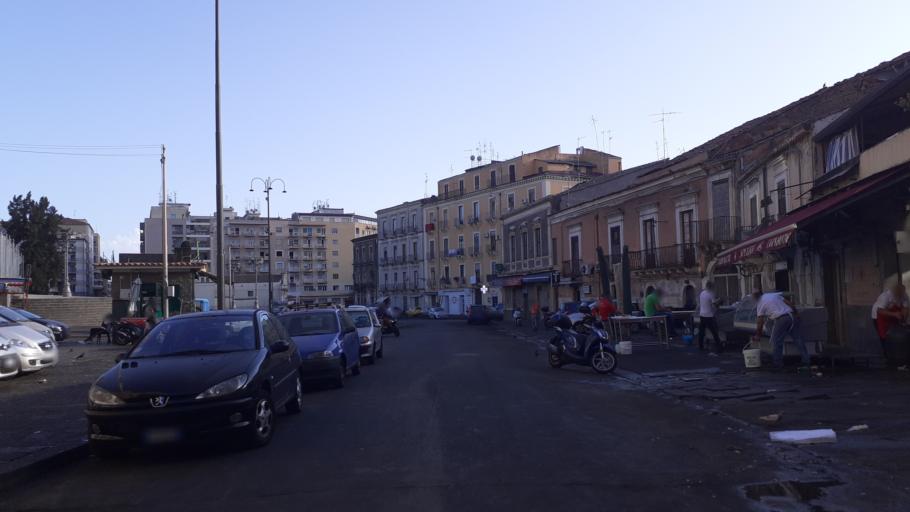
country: IT
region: Sicily
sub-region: Catania
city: Catania
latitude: 37.5106
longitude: 15.0883
